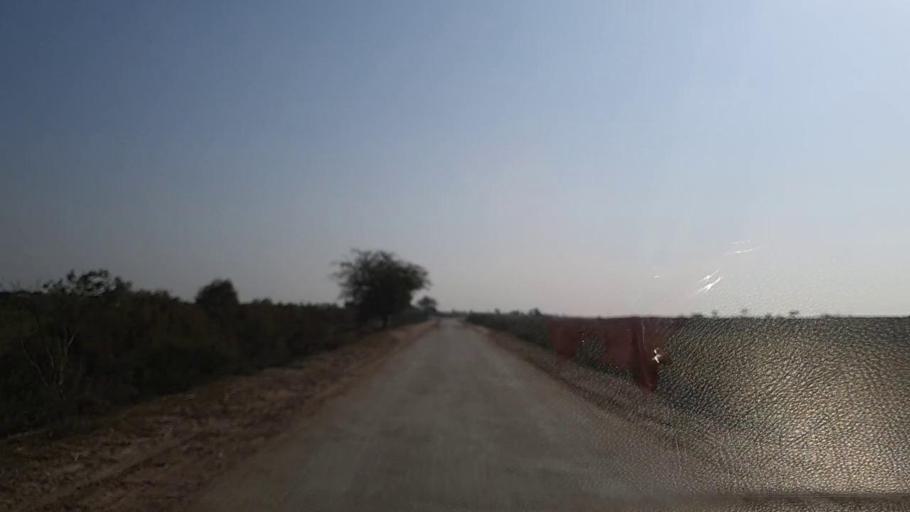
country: PK
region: Sindh
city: Sanghar
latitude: 25.9936
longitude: 69.0240
